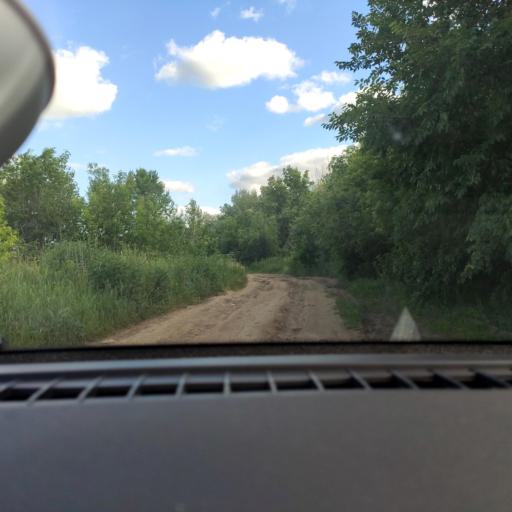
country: RU
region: Samara
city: Samara
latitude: 53.1786
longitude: 50.2370
